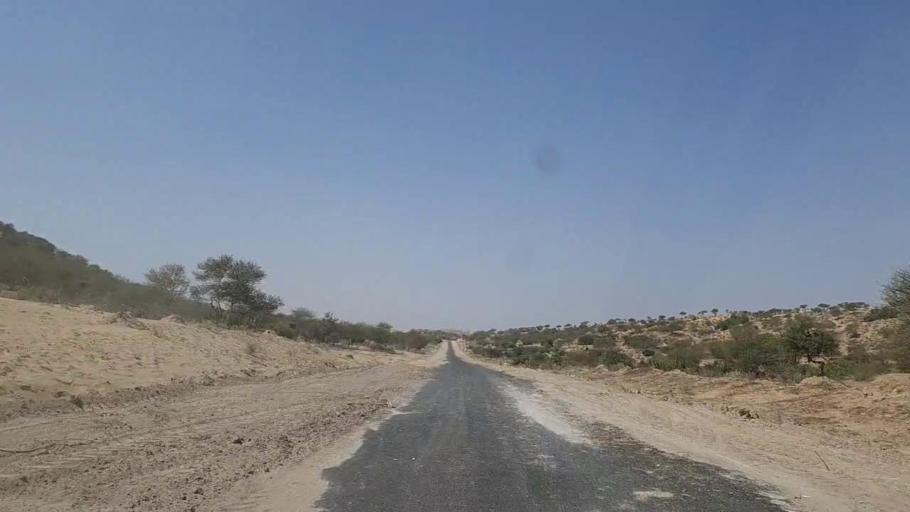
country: PK
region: Sindh
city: Diplo
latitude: 24.5882
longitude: 69.5446
